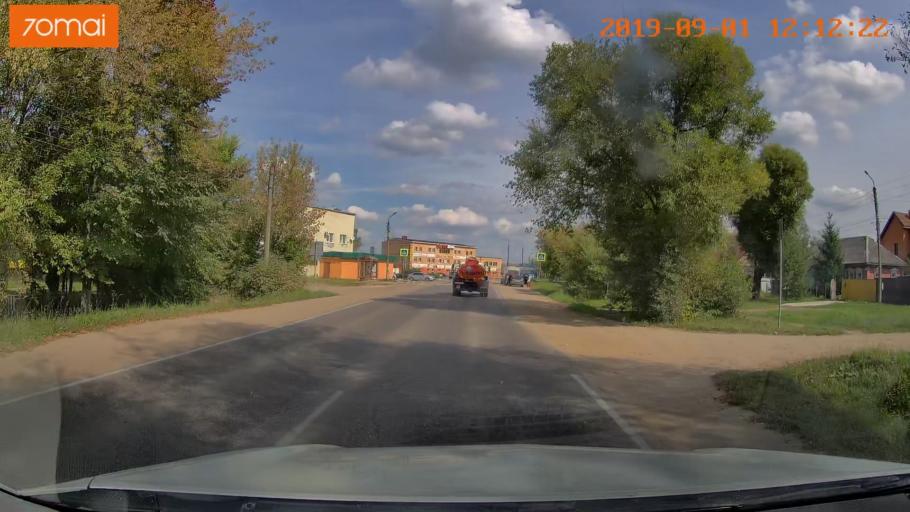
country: RU
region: Kaluga
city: Maloyaroslavets
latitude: 55.0045
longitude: 36.4444
